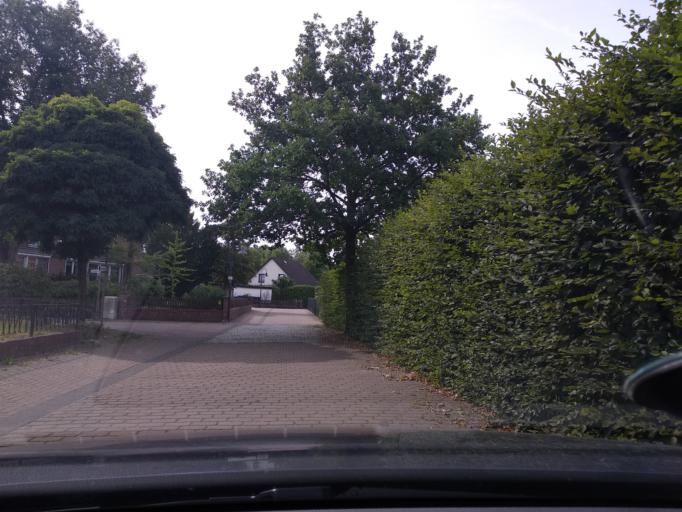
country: DE
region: Lower Saxony
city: Wagenhoff
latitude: 52.5112
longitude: 10.4698
